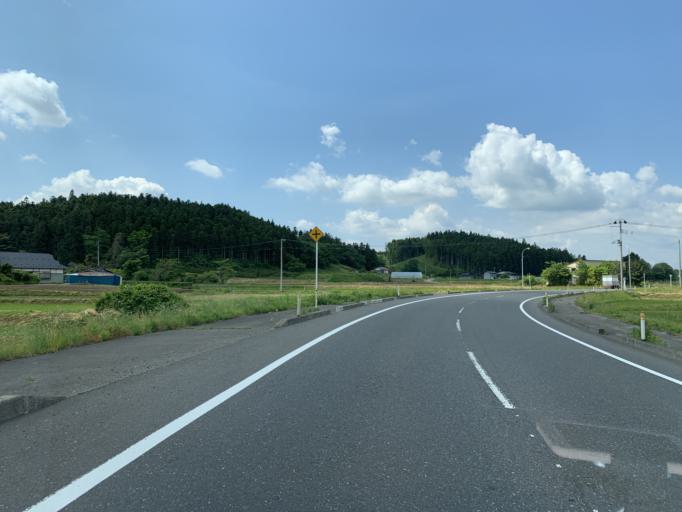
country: JP
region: Miyagi
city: Furukawa
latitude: 38.7307
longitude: 140.9576
